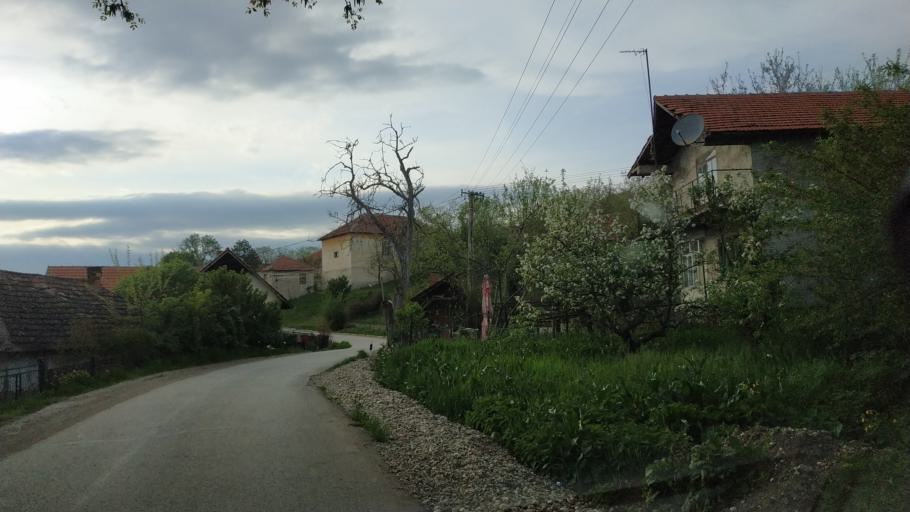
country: RS
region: Central Serbia
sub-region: Zajecarski Okrug
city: Soko Banja
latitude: 43.5276
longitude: 21.8553
